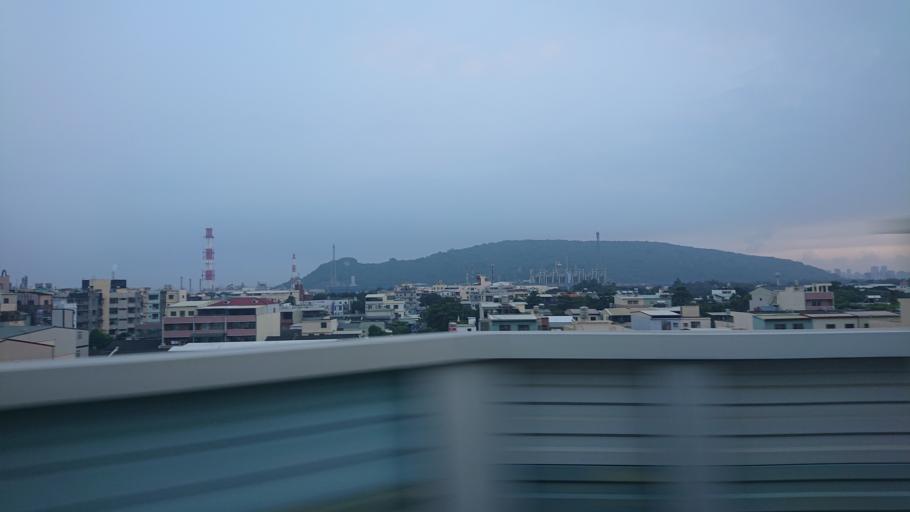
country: TW
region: Kaohsiung
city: Kaohsiung
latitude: 22.7188
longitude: 120.3082
